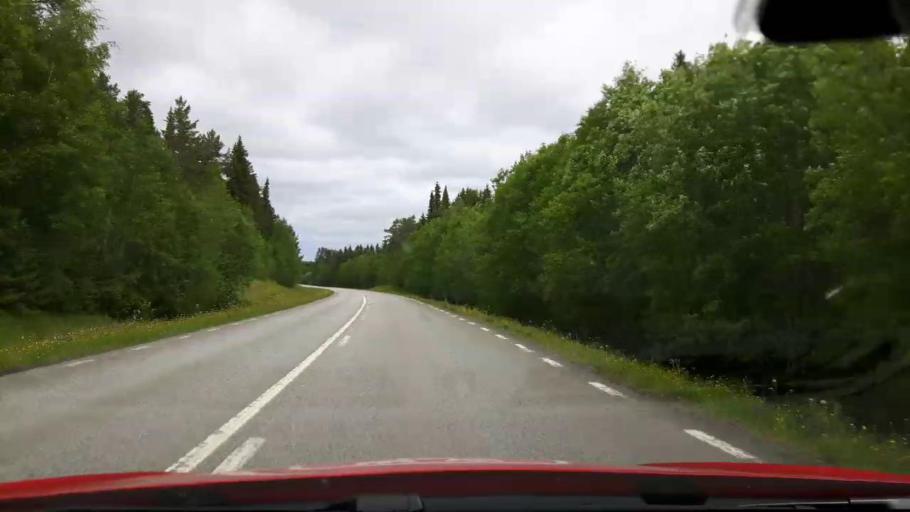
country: SE
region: Jaemtland
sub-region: Krokoms Kommun
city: Krokom
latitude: 63.3647
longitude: 14.5062
